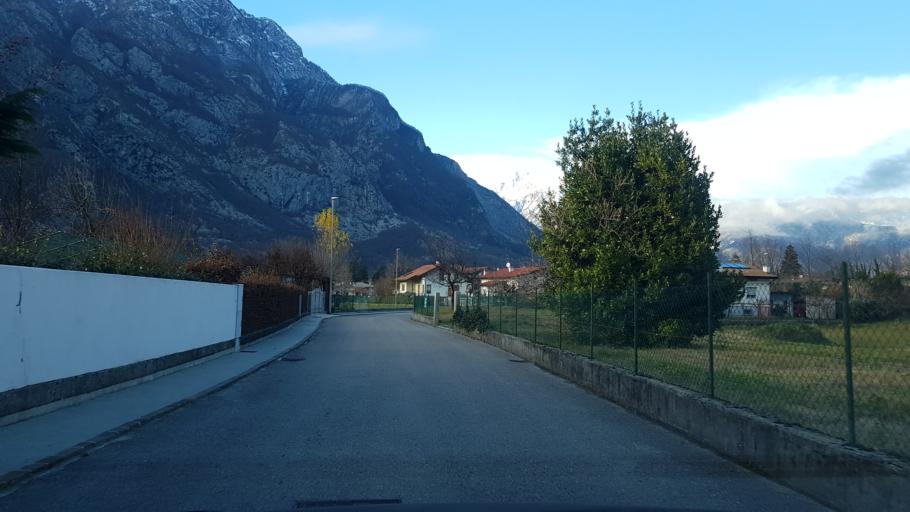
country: IT
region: Friuli Venezia Giulia
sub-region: Provincia di Udine
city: Venzone
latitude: 46.3278
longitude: 13.1389
